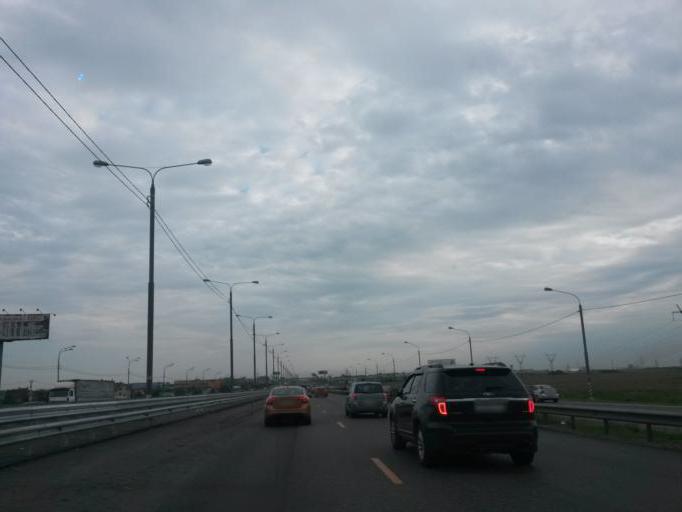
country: RU
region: Moskovskaya
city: Shcherbinka
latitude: 55.4579
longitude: 37.6190
